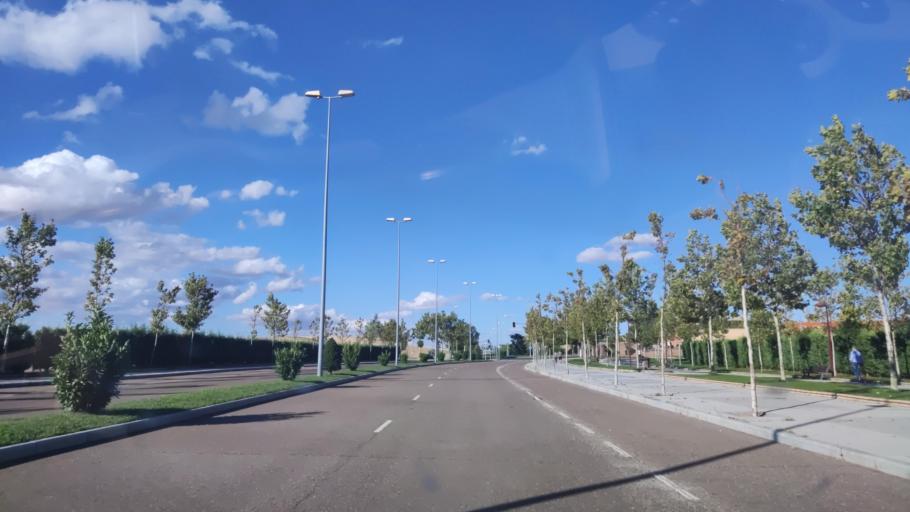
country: ES
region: Castille and Leon
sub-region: Provincia de Salamanca
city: Salamanca
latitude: 40.9751
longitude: -5.6858
